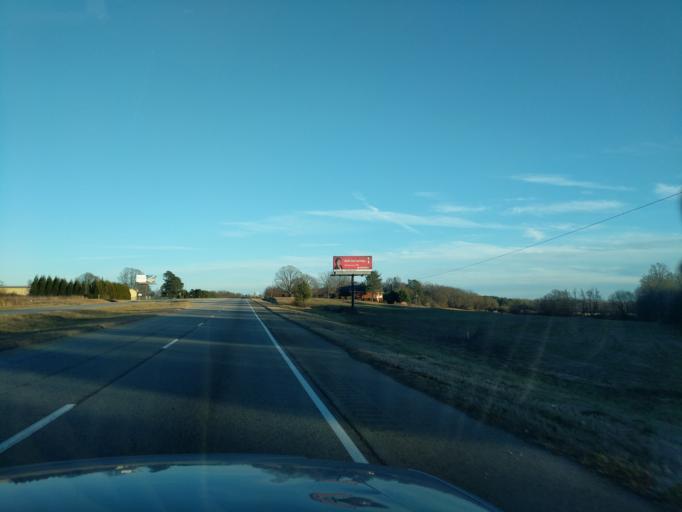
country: US
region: Georgia
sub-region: Franklin County
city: Lavonia
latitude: 34.4550
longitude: -83.1566
